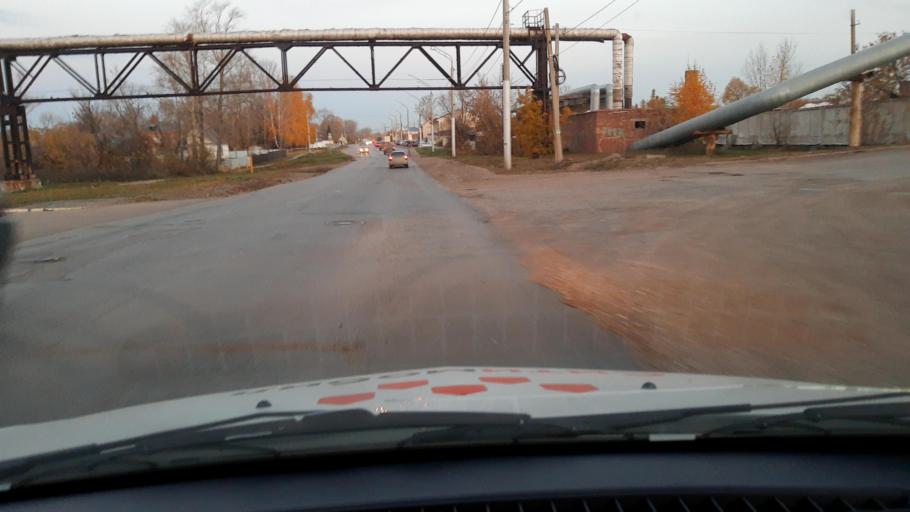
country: RU
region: Bashkortostan
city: Iglino
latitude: 54.7625
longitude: 56.2409
